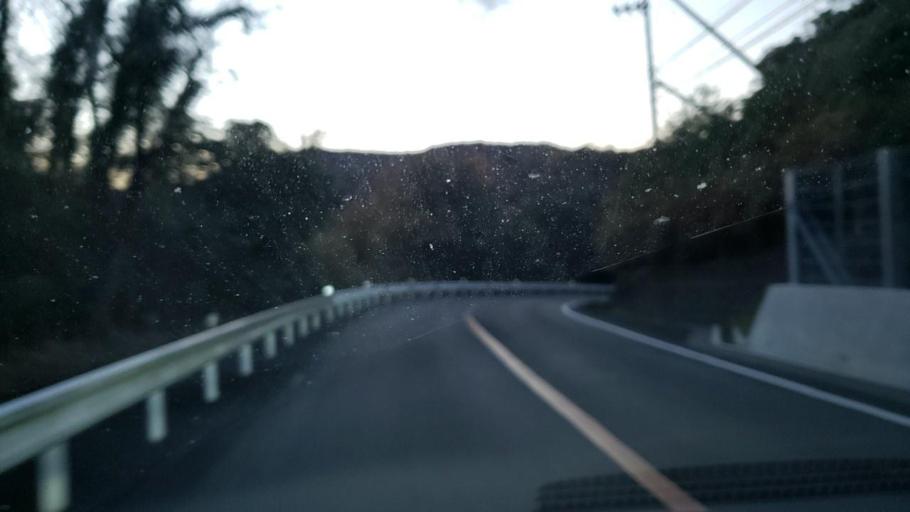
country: JP
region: Hyogo
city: Fukura
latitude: 34.2823
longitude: 134.6815
